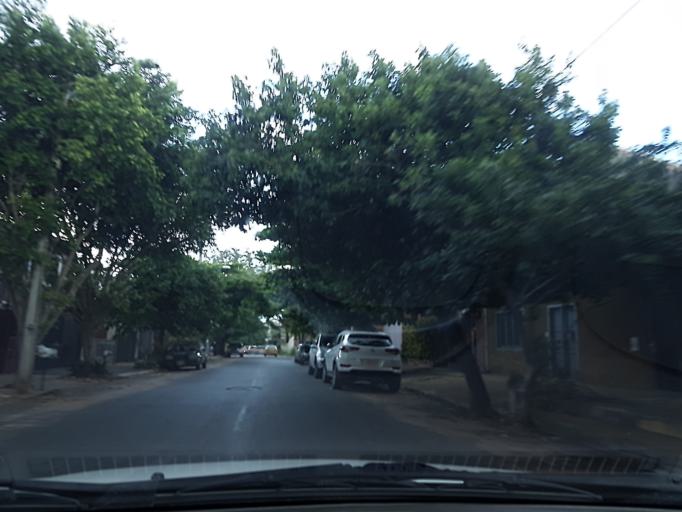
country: PY
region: Central
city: Fernando de la Mora
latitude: -25.2934
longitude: -57.5637
